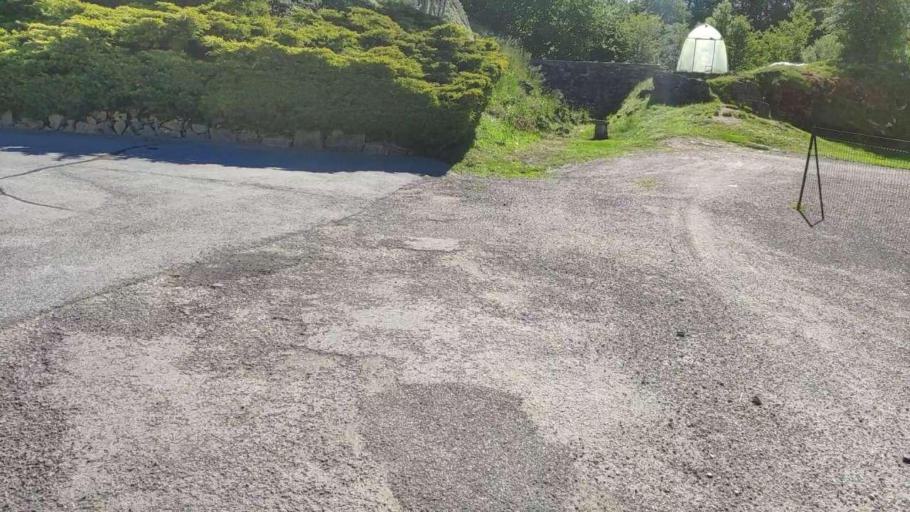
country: FR
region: Franche-Comte
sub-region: Departement du Jura
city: Perrigny
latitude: 46.6890
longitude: 5.6641
